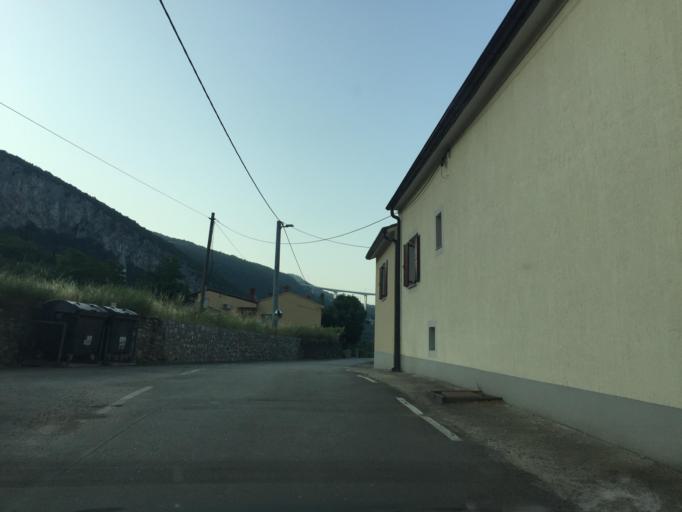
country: IT
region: Friuli Venezia Giulia
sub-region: Provincia di Trieste
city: Dolina
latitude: 45.5739
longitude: 13.8542
